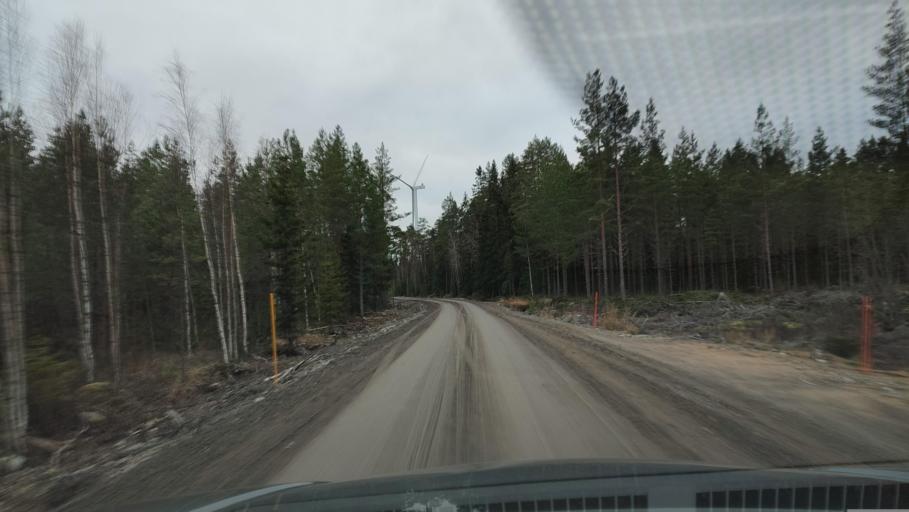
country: FI
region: Southern Ostrobothnia
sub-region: Suupohja
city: Karijoki
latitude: 62.1973
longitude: 21.5897
